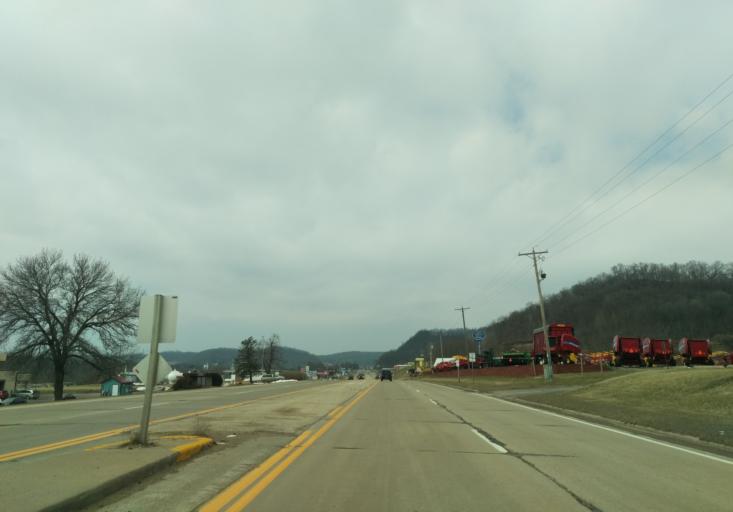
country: US
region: Wisconsin
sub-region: Richland County
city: Richland Center
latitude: 43.3184
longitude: -90.3615
